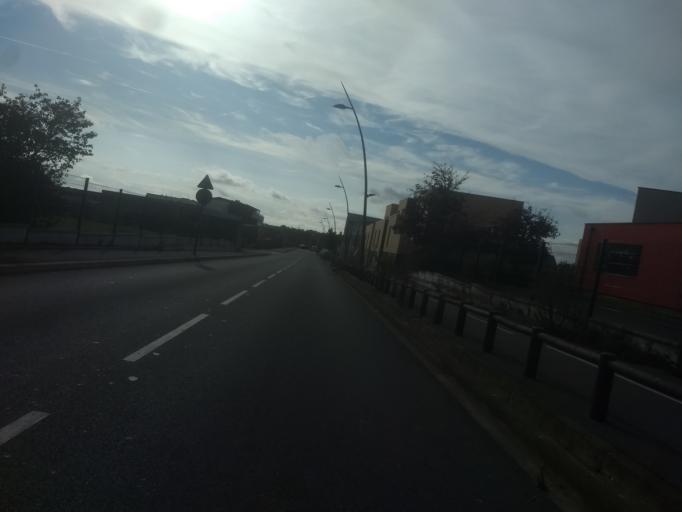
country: FR
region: Nord-Pas-de-Calais
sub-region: Departement du Pas-de-Calais
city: Dainville
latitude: 50.2909
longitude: 2.7356
